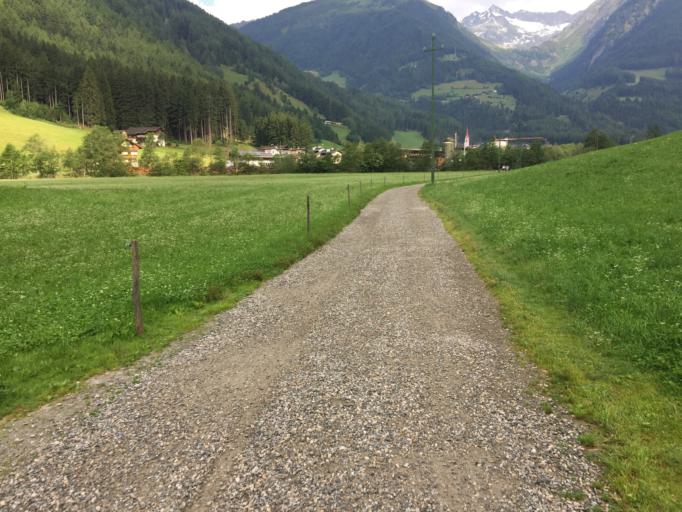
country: IT
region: Trentino-Alto Adige
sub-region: Bolzano
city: Molini di Tures
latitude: 46.9437
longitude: 11.9266
